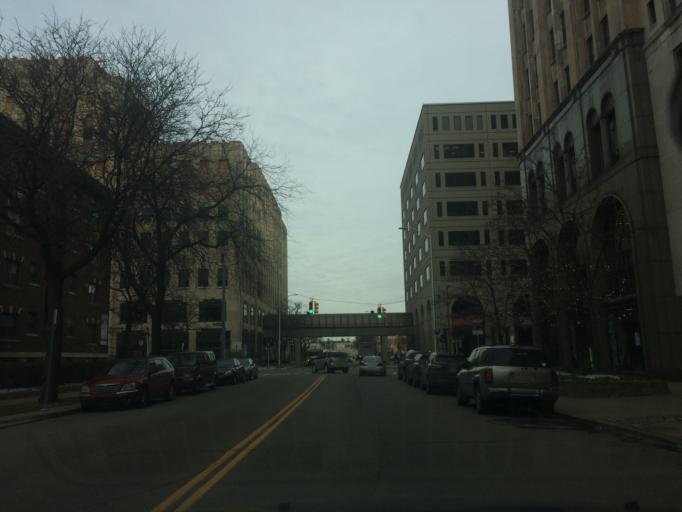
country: US
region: Michigan
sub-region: Wayne County
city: Hamtramck
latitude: 42.3702
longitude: -83.0778
